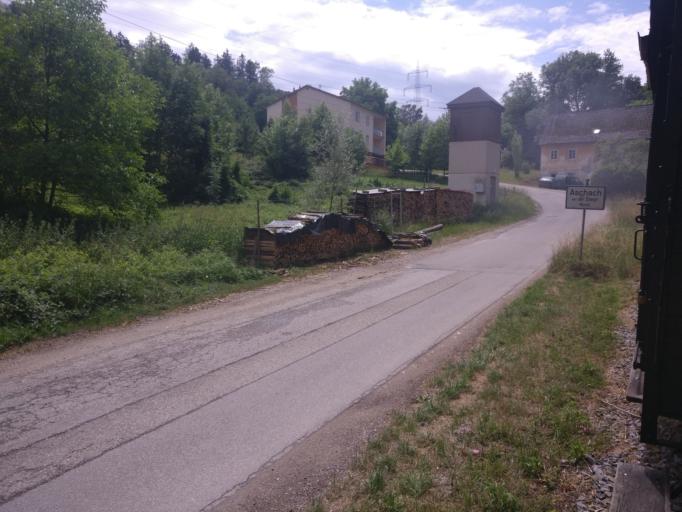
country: AT
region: Upper Austria
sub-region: Politischer Bezirk Steyr-Land
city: Sierning
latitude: 48.0301
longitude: 14.3371
